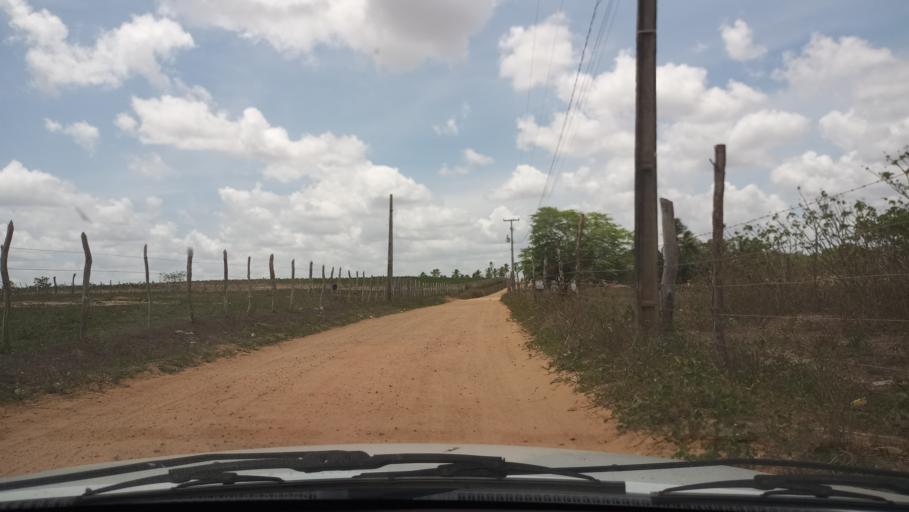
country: BR
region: Rio Grande do Norte
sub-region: Brejinho
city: Brejinho
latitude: -6.3037
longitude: -35.3454
